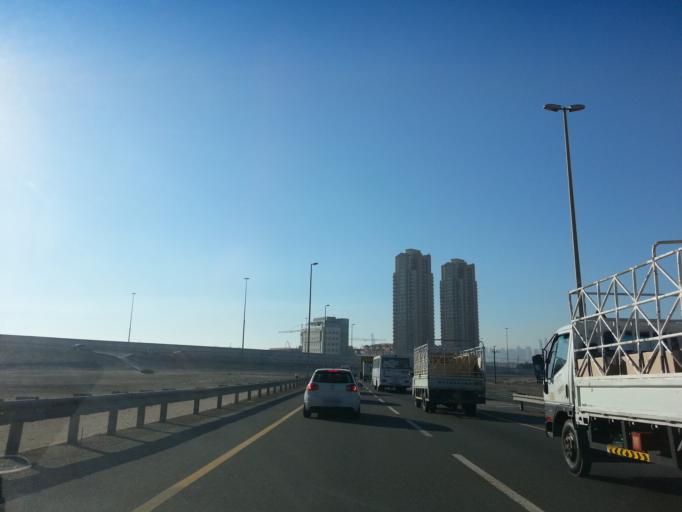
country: AE
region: Dubai
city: Dubai
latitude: 25.0454
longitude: 55.2005
